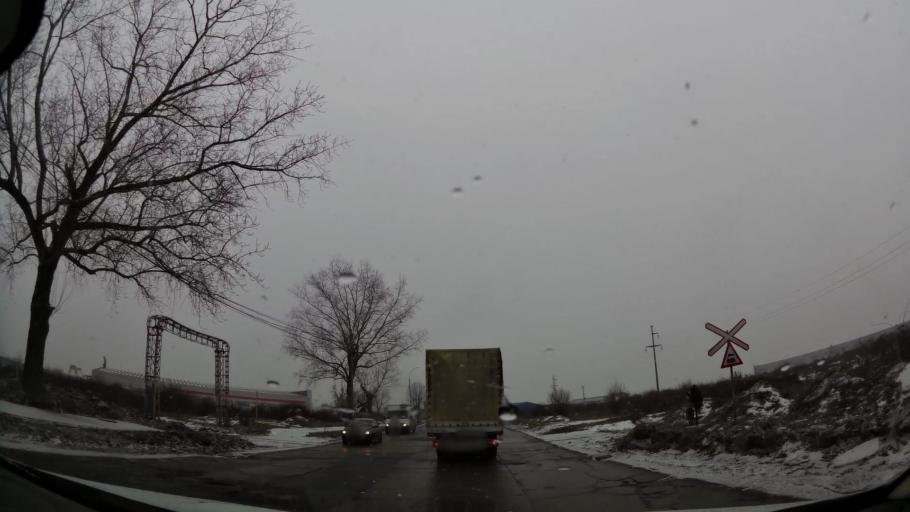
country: RO
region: Dambovita
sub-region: Municipiul Targoviste
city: Targoviste
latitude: 44.9237
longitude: 25.4328
